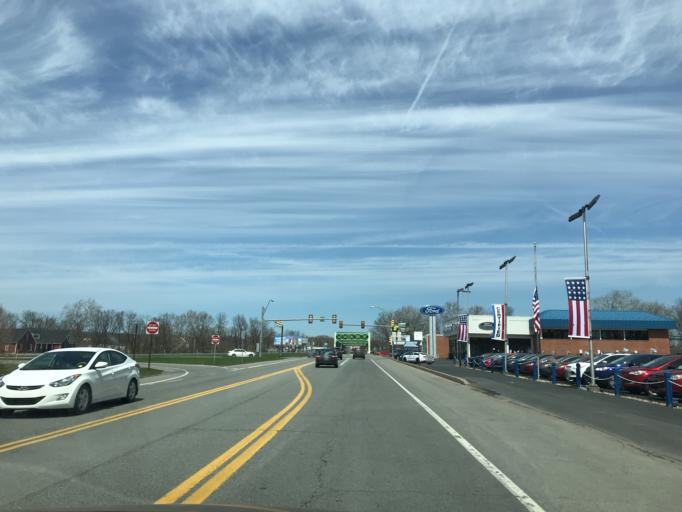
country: US
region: Pennsylvania
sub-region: Snyder County
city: Selinsgrove
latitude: 40.8109
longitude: -76.8563
